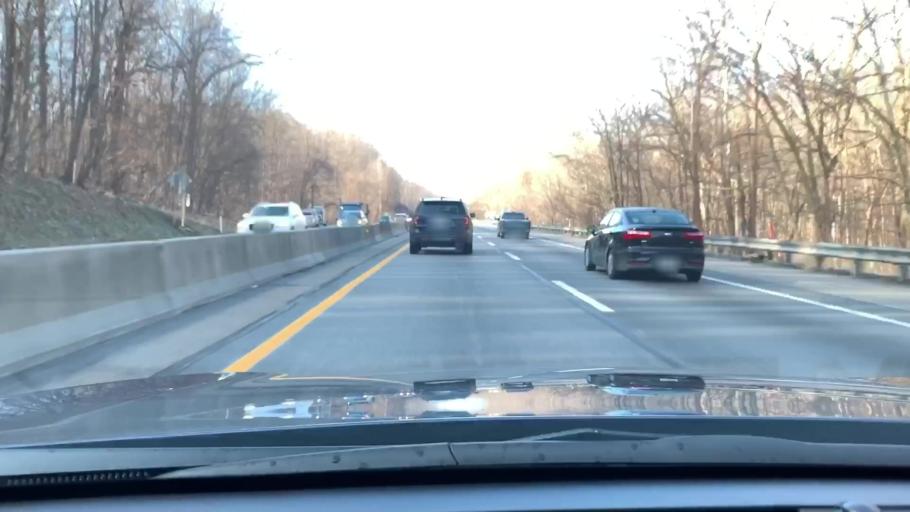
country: US
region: Pennsylvania
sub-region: Chester County
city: Downingtown
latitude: 40.0969
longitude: -75.7393
